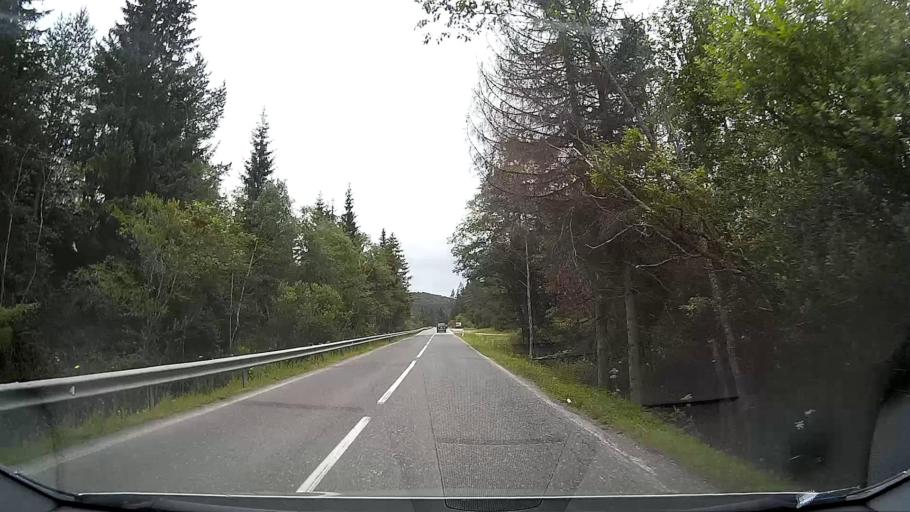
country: SK
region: Kosicky
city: Dobsina
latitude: 48.8832
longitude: 20.2358
